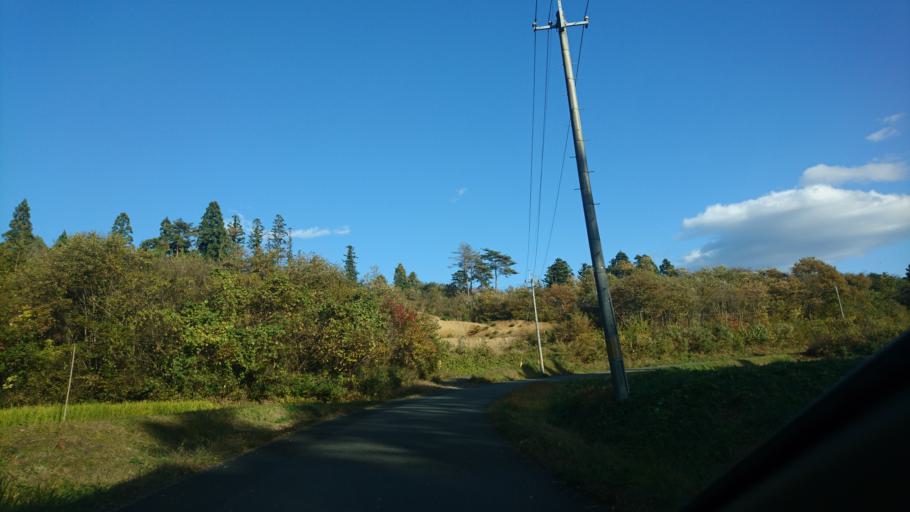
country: JP
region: Iwate
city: Ichinoseki
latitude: 38.9218
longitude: 141.2128
